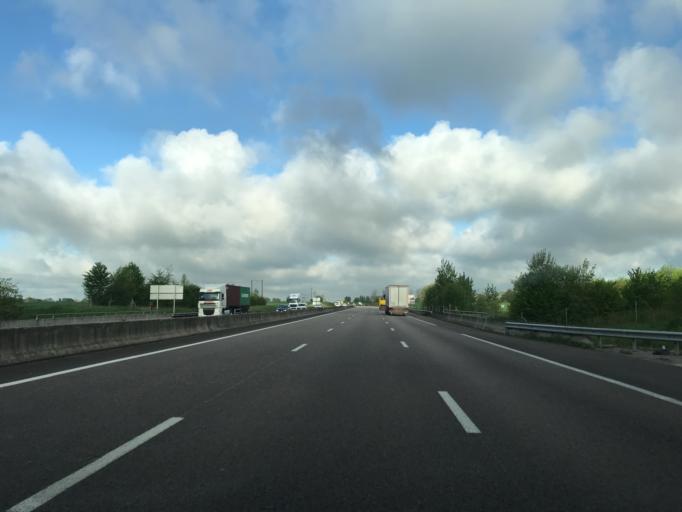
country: FR
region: Haute-Normandie
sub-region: Departement de l'Eure
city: Hauville
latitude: 49.3687
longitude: 0.7799
